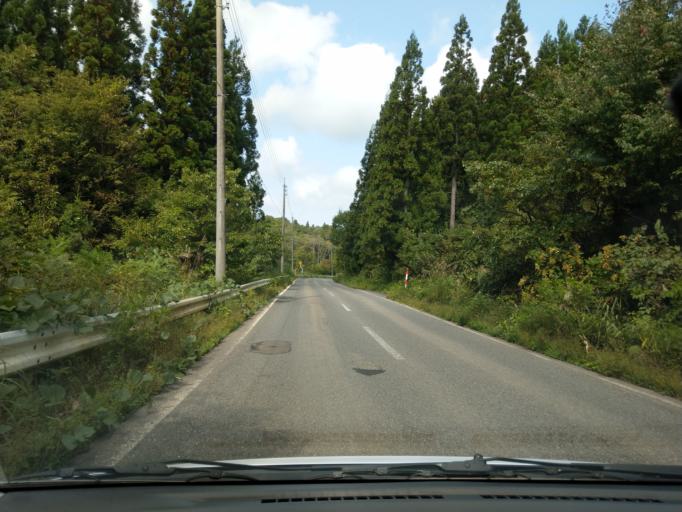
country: JP
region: Akita
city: Omagari
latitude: 39.4611
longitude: 140.3179
